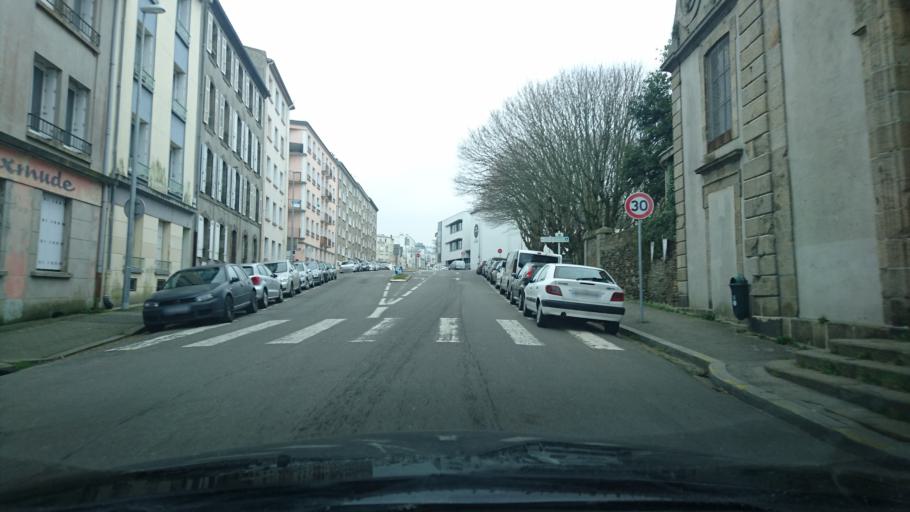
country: FR
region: Brittany
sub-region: Departement du Finistere
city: Brest
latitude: 48.3822
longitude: -4.5009
